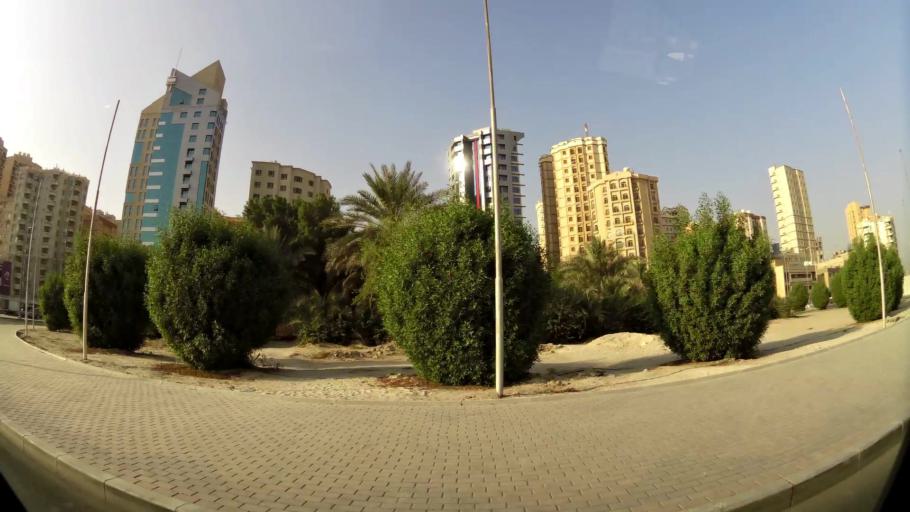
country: KW
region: Muhafazat Hawalli
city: Hawalli
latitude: 29.3423
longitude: 48.0401
